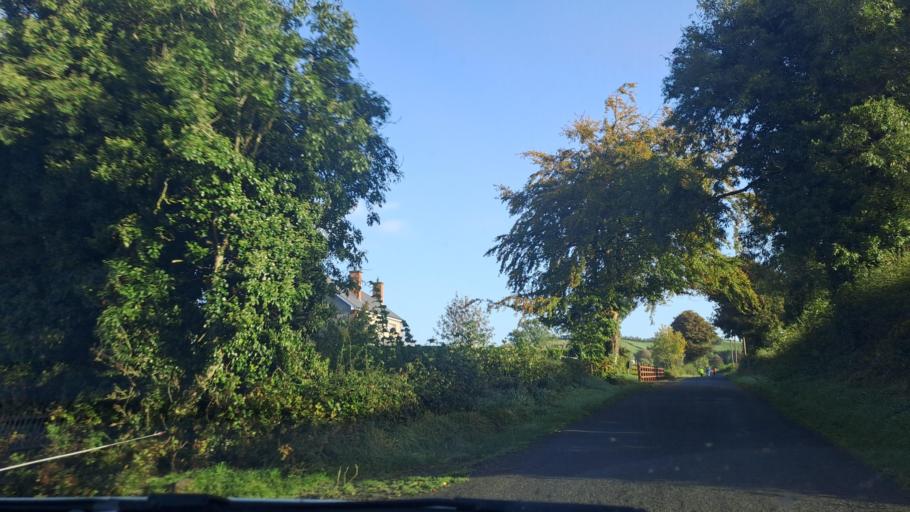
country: IE
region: Ulster
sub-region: County Monaghan
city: Castleblayney
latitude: 54.0466
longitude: -6.8514
